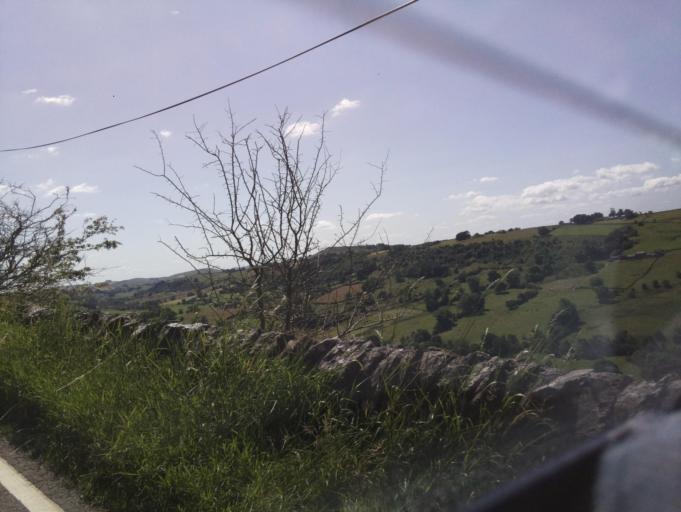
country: GB
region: England
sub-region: Derbyshire
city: Buxton
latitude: 53.1823
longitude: -1.8444
